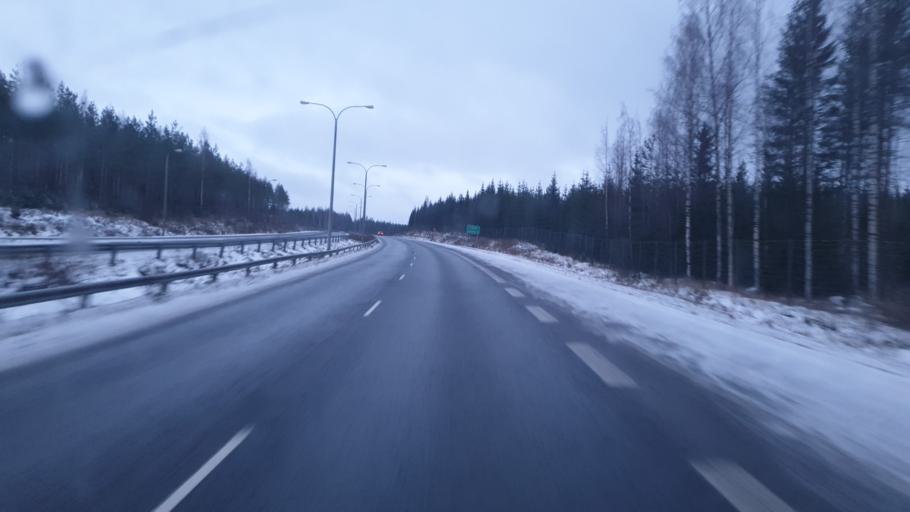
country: FI
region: Northern Savo
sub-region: Kuopio
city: Siilinjaervi
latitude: 63.0161
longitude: 27.6663
